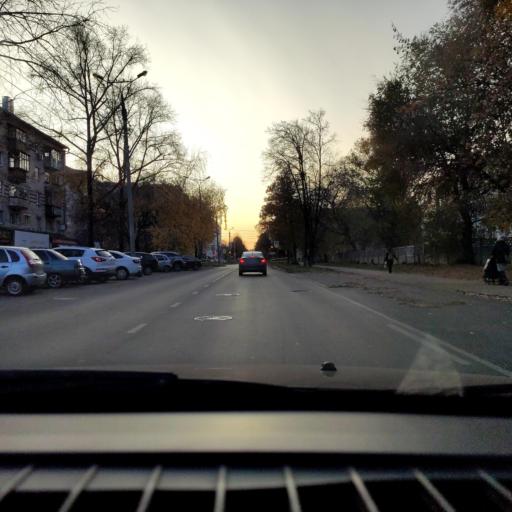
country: RU
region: Samara
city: Tol'yatti
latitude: 53.5057
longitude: 49.4148
